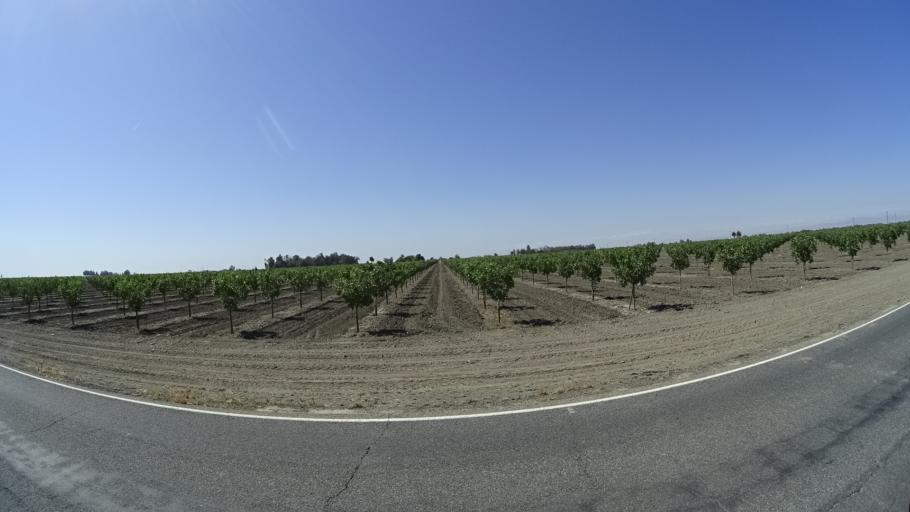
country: US
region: California
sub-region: Kings County
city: Stratford
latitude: 36.2114
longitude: -119.7945
